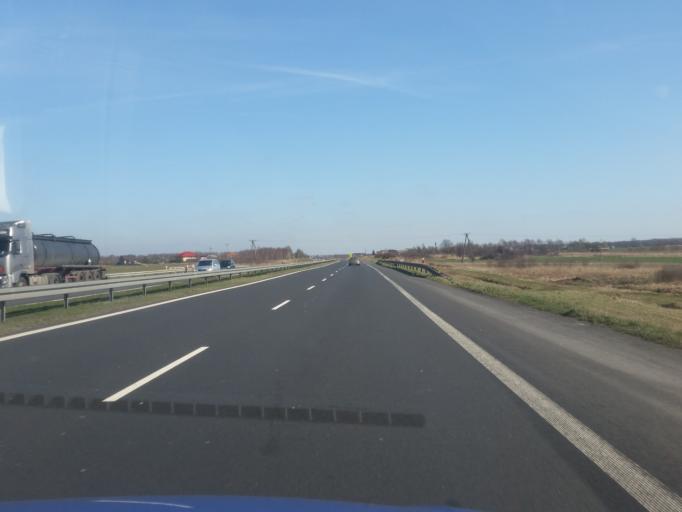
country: PL
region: Silesian Voivodeship
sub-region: Powiat czestochowski
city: Mykanow
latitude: 50.9166
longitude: 19.2172
